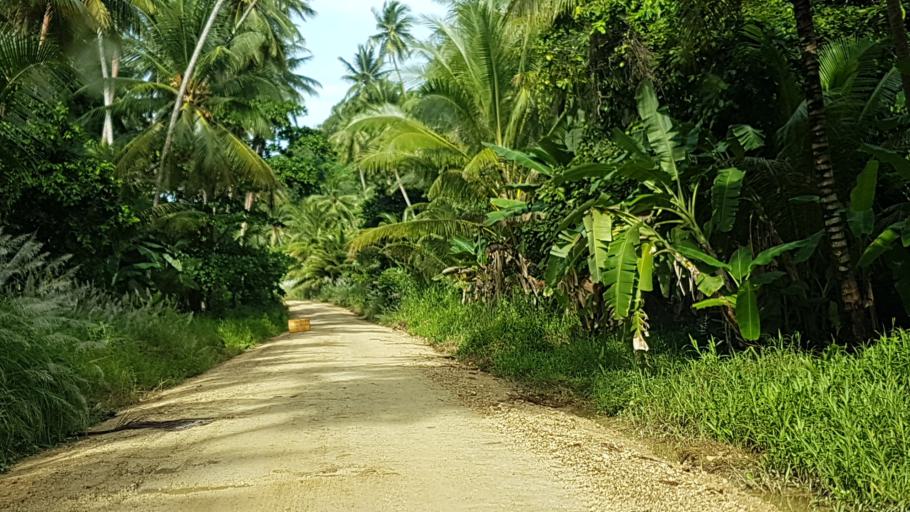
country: PG
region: Milne Bay
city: Alotau
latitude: -10.2956
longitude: 150.7656
